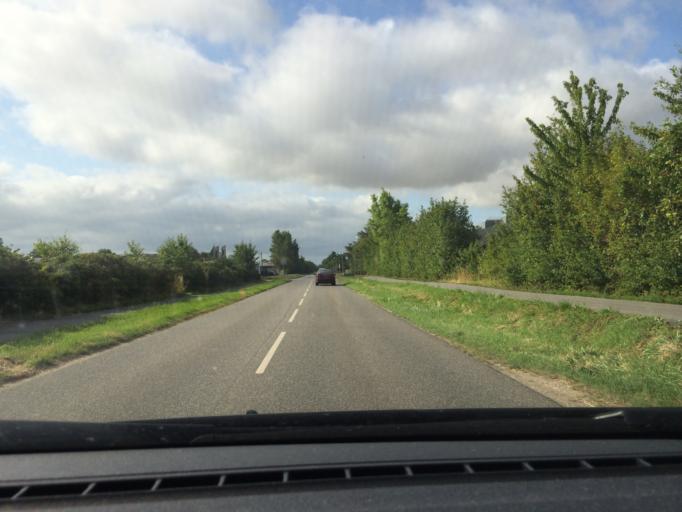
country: DK
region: Zealand
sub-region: Vordingborg Kommune
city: Stege
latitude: 54.9985
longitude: 12.2838
